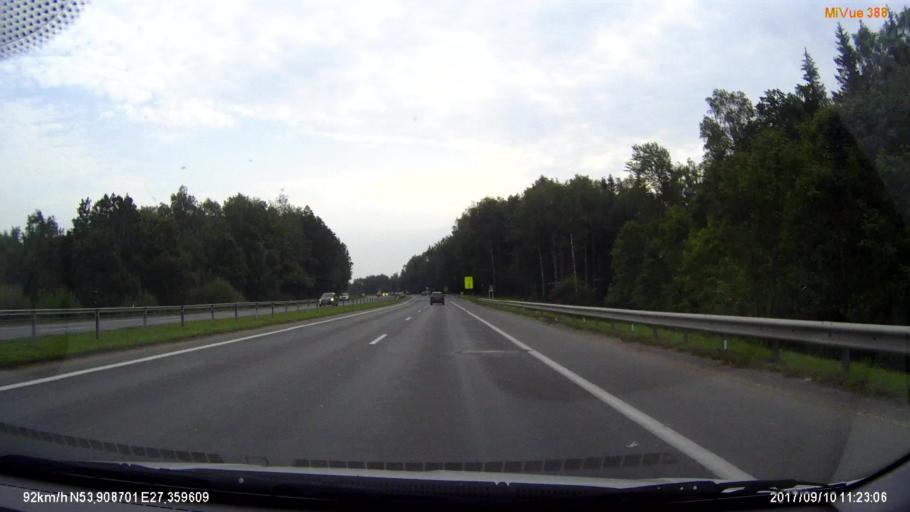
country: BY
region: Minsk
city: Khatsyezhyna
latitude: 53.9086
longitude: 27.3603
